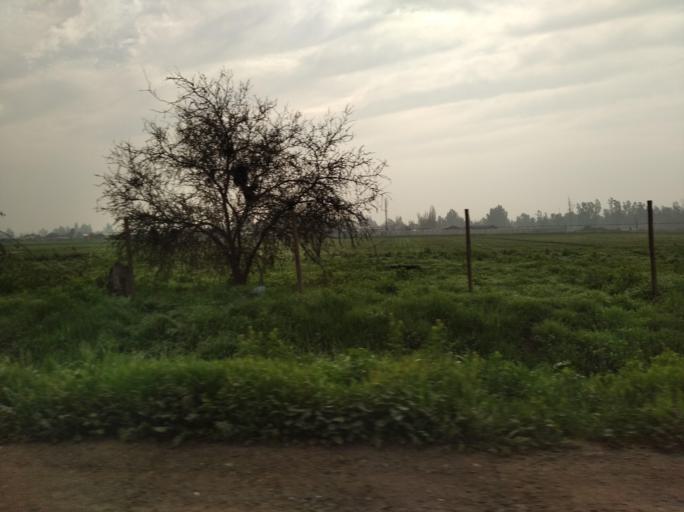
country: CL
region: Santiago Metropolitan
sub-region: Provincia de Chacabuco
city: Lampa
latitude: -33.3115
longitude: -70.8423
